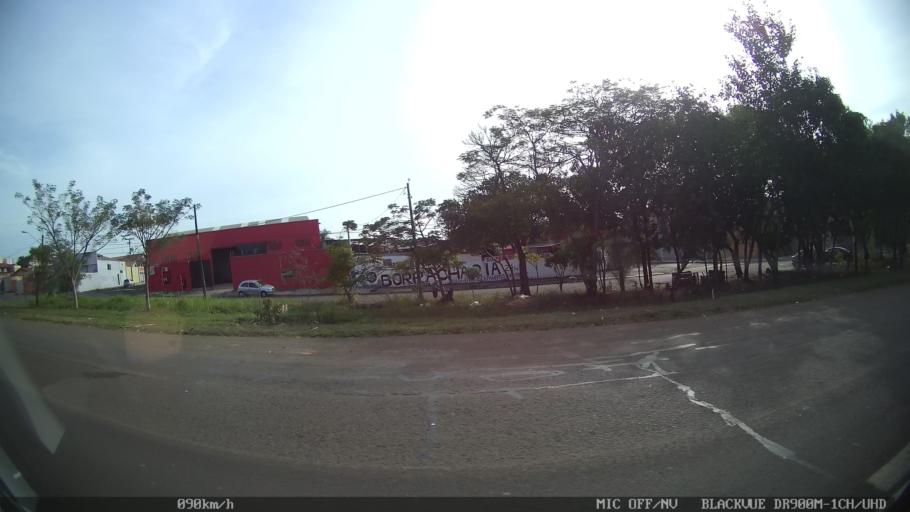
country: BR
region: Sao Paulo
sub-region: Piracicaba
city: Piracicaba
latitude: -22.6821
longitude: -47.6917
